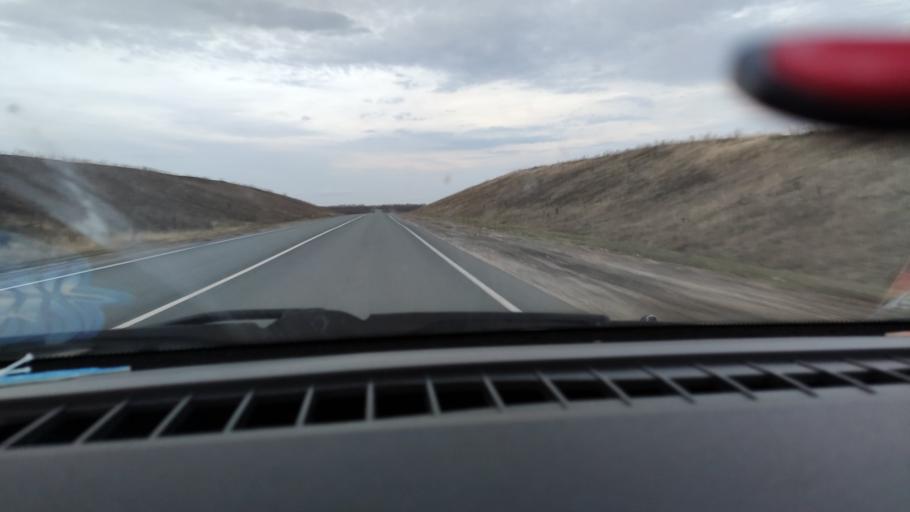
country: RU
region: Saratov
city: Sinodskoye
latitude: 51.9293
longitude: 46.5750
